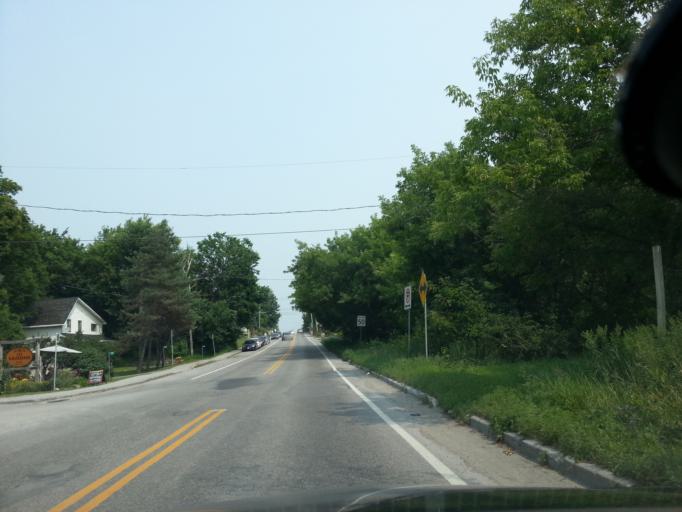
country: CA
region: Quebec
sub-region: Outaouais
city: Gatineau
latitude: 45.5030
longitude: -75.8103
